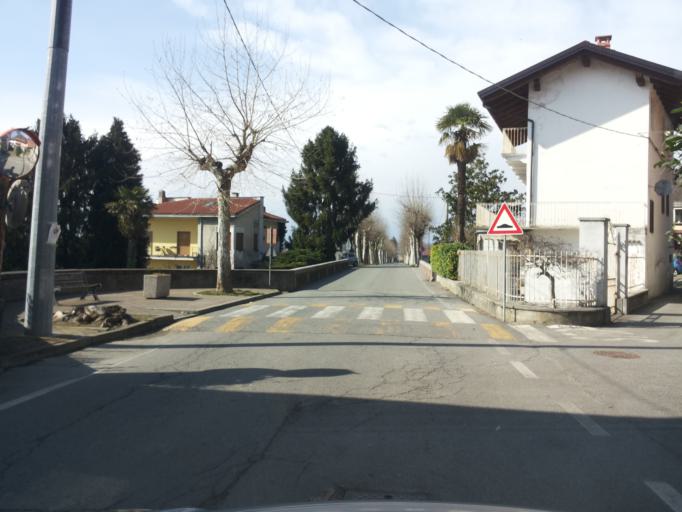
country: IT
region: Piedmont
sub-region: Provincia di Torino
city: Vestigne
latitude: 45.3879
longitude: 7.9523
